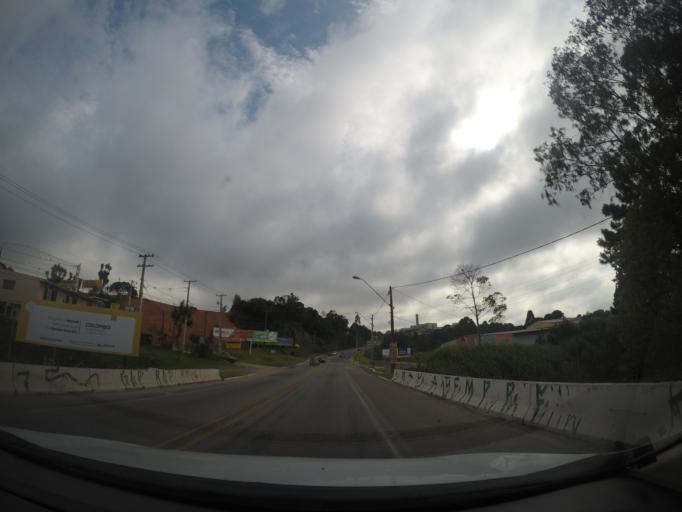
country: BR
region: Parana
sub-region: Colombo
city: Colombo
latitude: -25.3639
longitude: -49.2202
